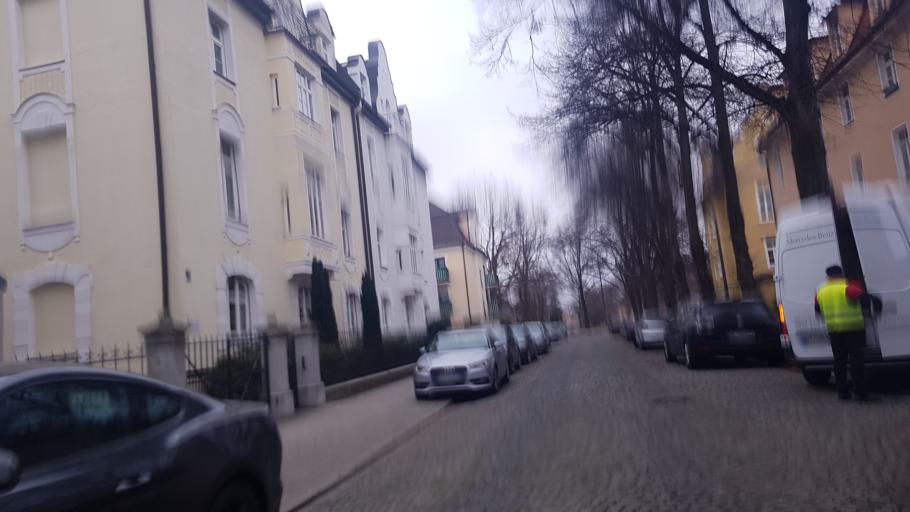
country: DE
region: Bavaria
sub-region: Upper Bavaria
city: Munich
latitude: 48.1576
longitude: 11.5166
